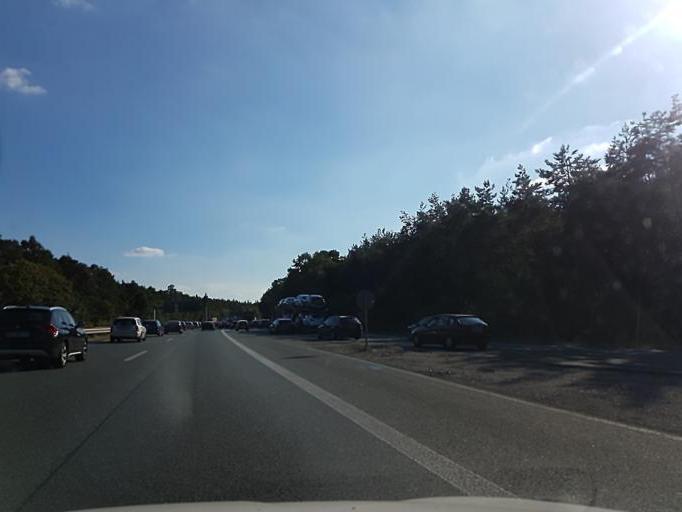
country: DE
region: Hesse
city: Raunheim
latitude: 50.0175
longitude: 8.4967
